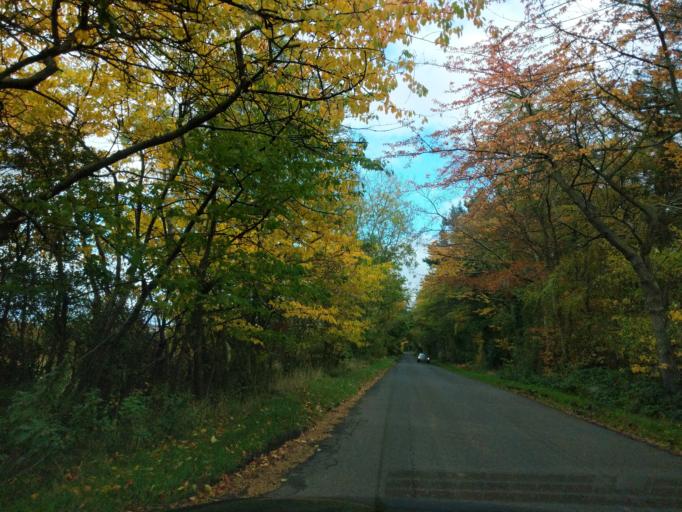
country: GB
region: Scotland
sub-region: East Lothian
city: Haddington
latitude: 55.9365
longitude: -2.7276
